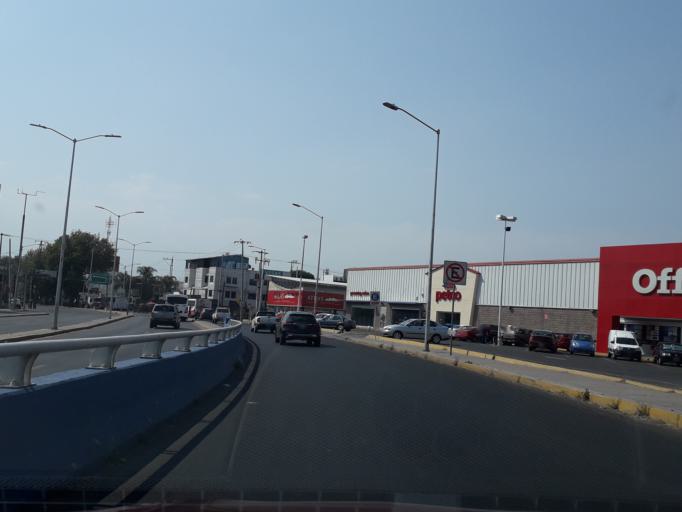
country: MX
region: Puebla
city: Puebla
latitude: 19.0389
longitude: -98.2257
